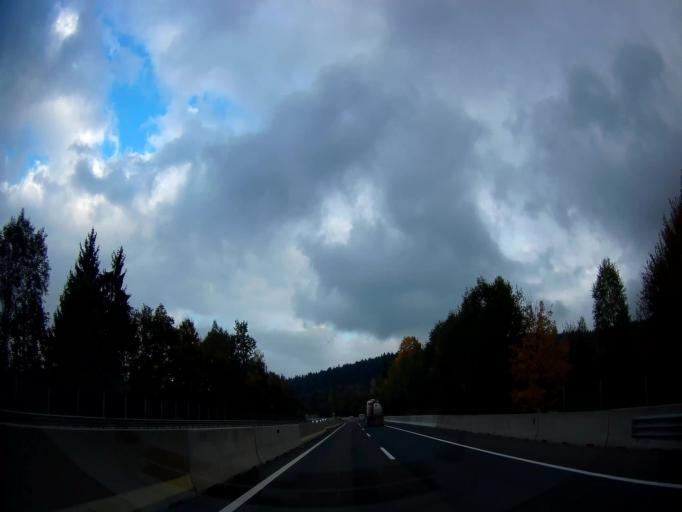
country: AT
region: Styria
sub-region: Politischer Bezirk Voitsberg
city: Ligist
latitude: 46.9782
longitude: 15.1718
